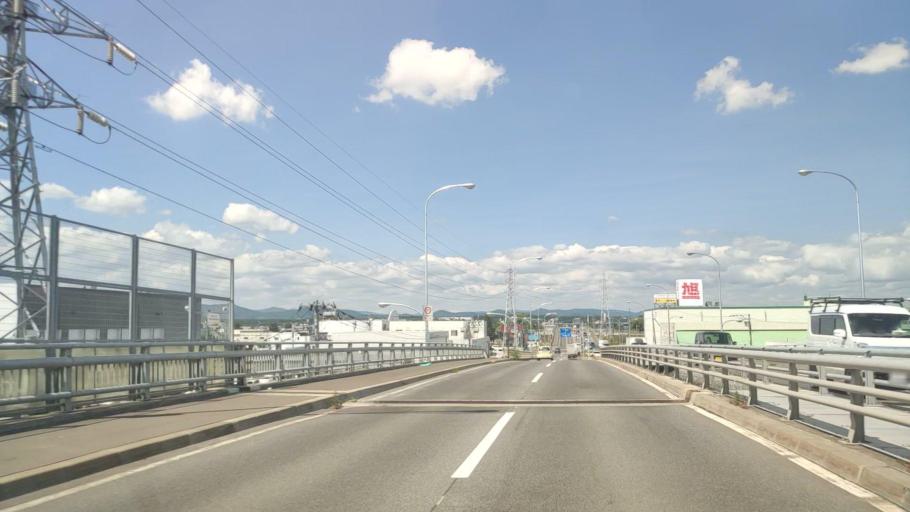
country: JP
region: Hokkaido
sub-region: Asahikawa-shi
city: Asahikawa
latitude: 43.7938
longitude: 142.4009
